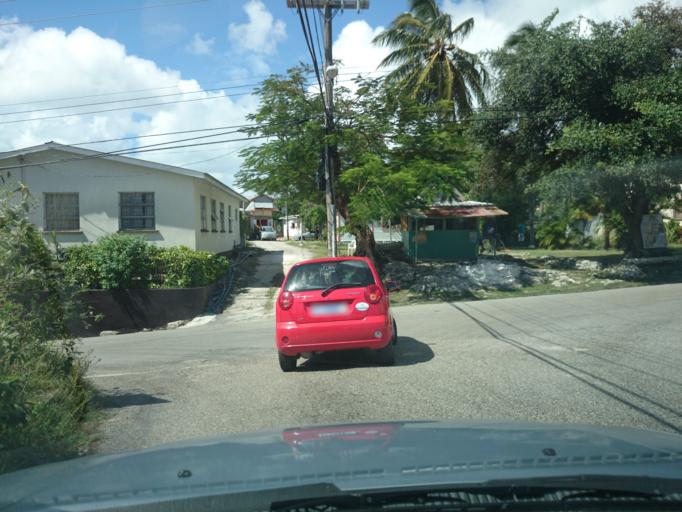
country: BB
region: Christ Church
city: Oistins
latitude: 13.0750
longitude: -59.5589
